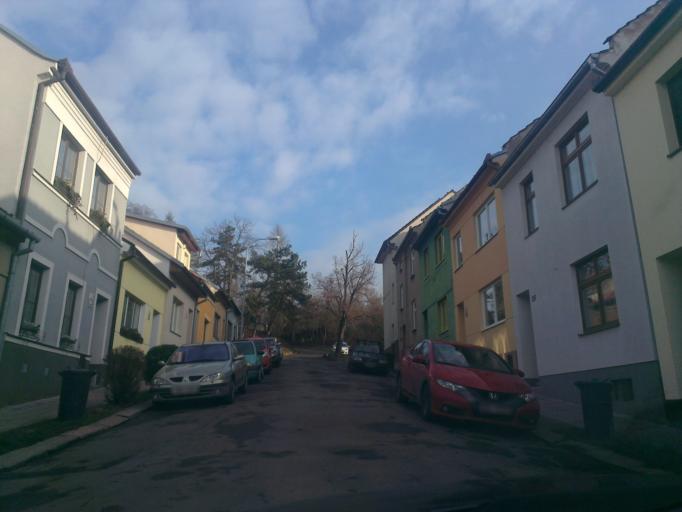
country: CZ
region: South Moravian
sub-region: Mesto Brno
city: Brno
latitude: 49.2031
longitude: 16.6454
